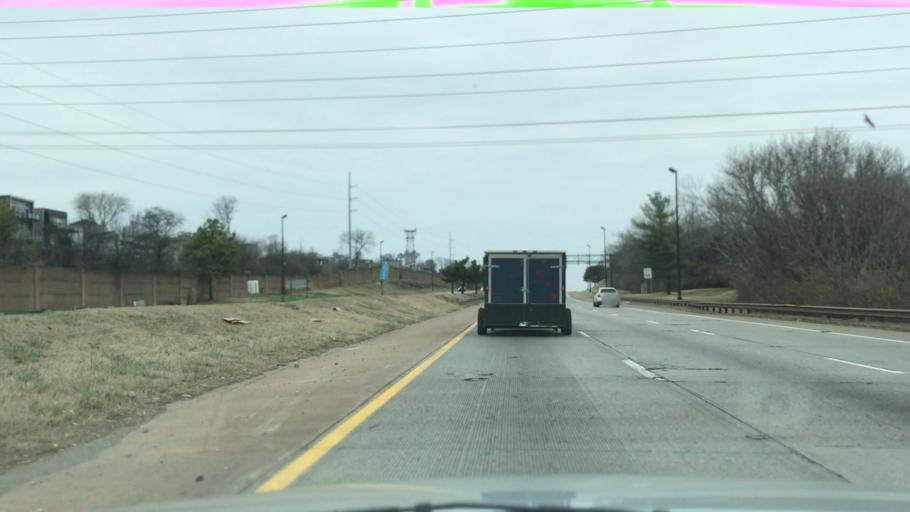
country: US
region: Tennessee
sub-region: Davidson County
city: Nashville
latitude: 36.1484
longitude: -86.8223
